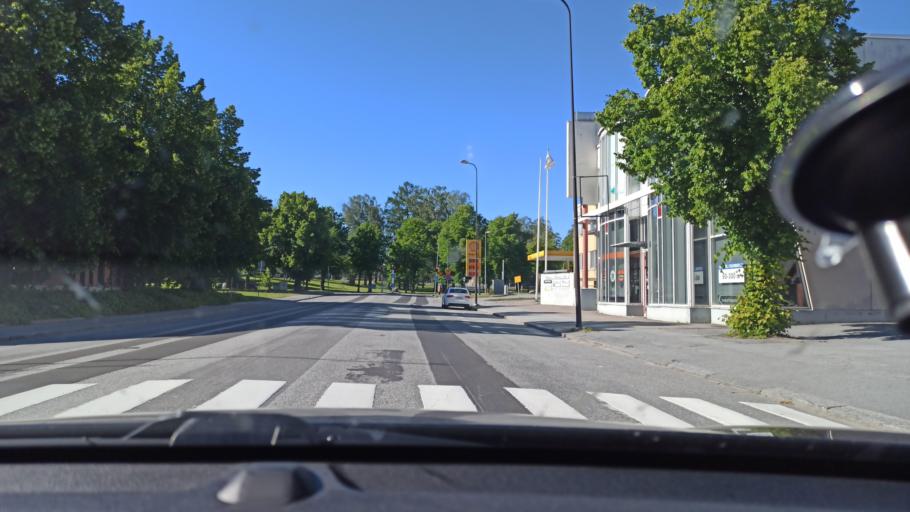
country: FI
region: Ostrobothnia
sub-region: Jakobstadsregionen
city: Jakobstad
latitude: 63.6759
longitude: 22.7114
